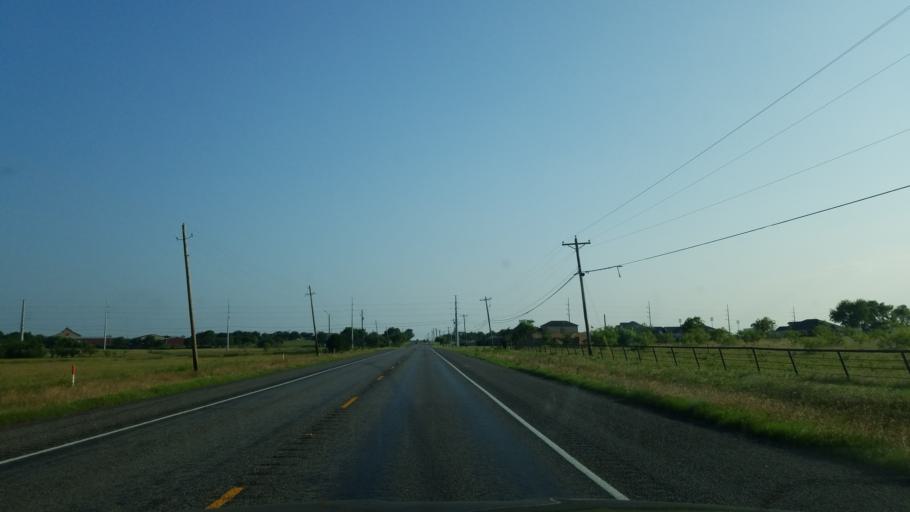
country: US
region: Texas
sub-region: Denton County
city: Denton
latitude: 33.2678
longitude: -97.1026
